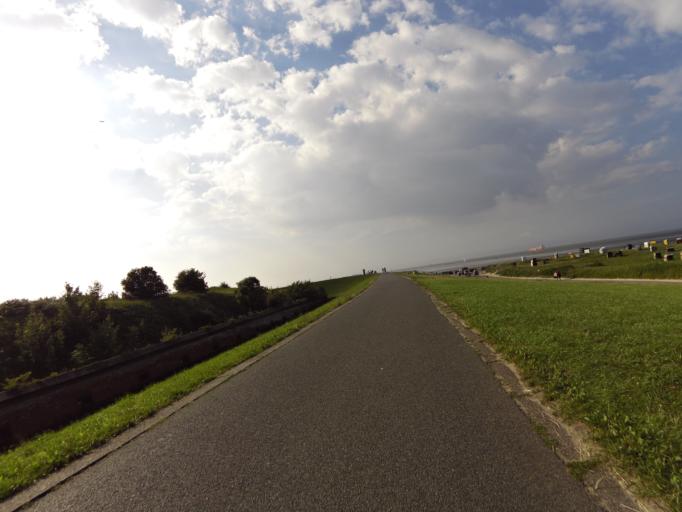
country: DE
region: Lower Saxony
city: Cuxhaven
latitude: 53.8906
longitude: 8.6826
